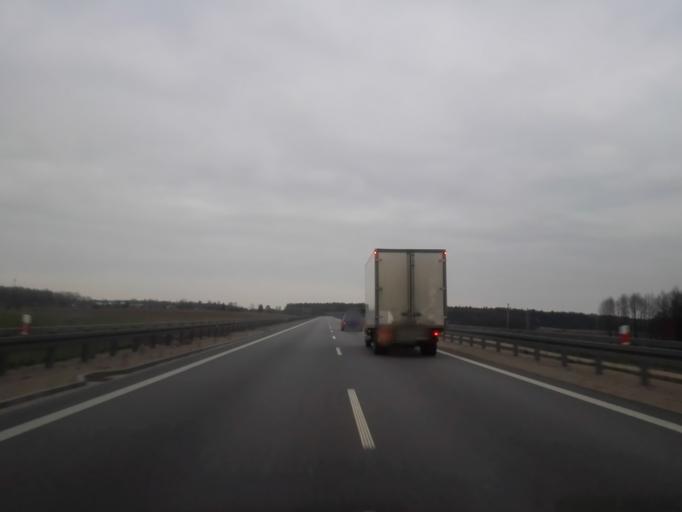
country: PL
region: Podlasie
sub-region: Powiat kolnenski
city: Stawiski
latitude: 53.3698
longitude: 22.1502
